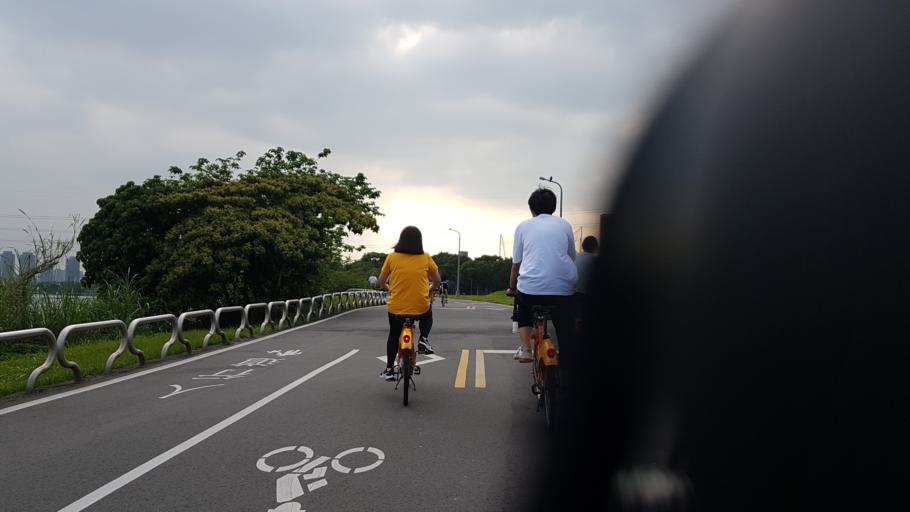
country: TW
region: Taipei
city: Taipei
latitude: 25.0228
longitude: 121.5118
